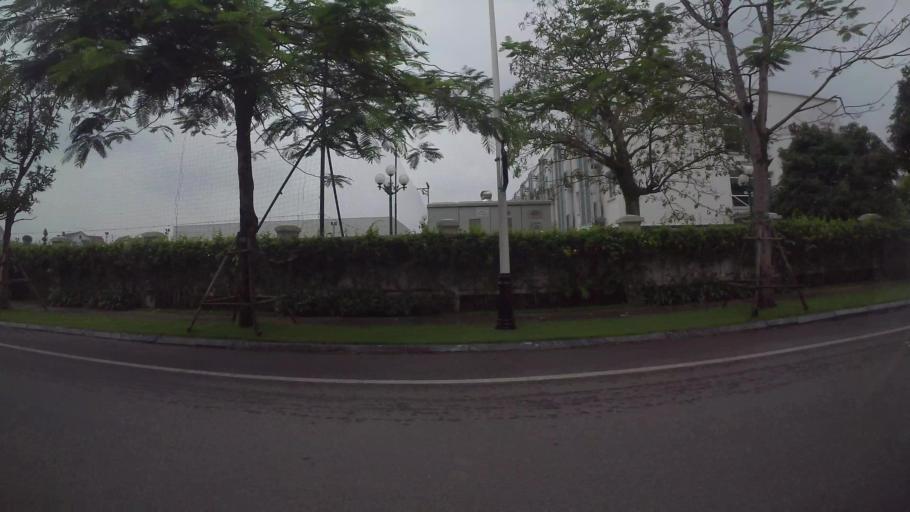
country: VN
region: Ha Noi
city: Trau Quy
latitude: 21.0442
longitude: 105.9196
